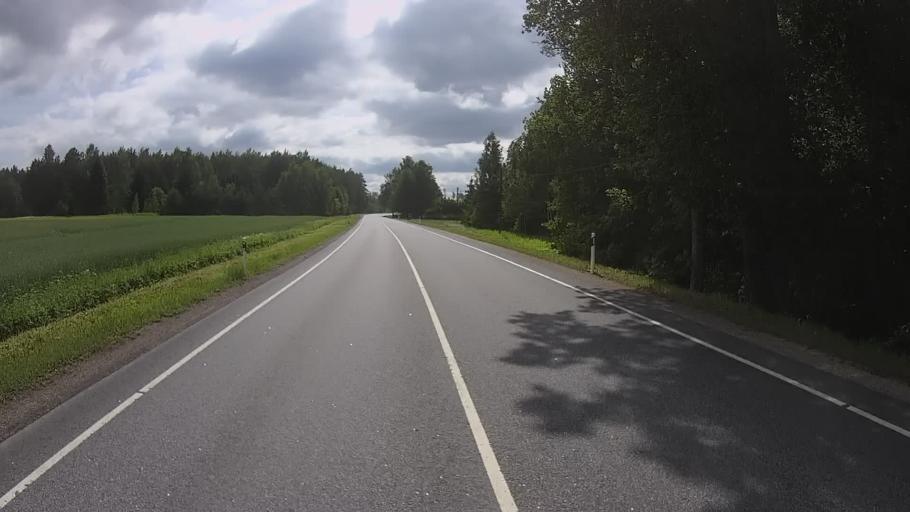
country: EE
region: Polvamaa
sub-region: Polva linn
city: Polva
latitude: 58.1447
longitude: 26.9448
